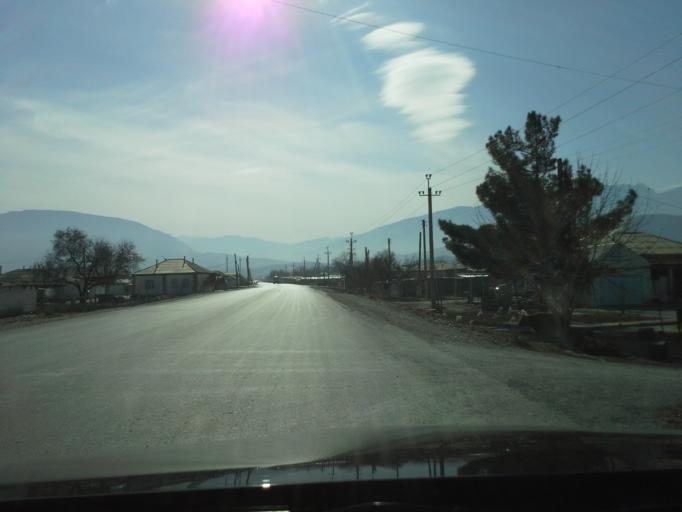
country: TM
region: Ahal
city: Abadan
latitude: 38.0850
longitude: 58.0187
